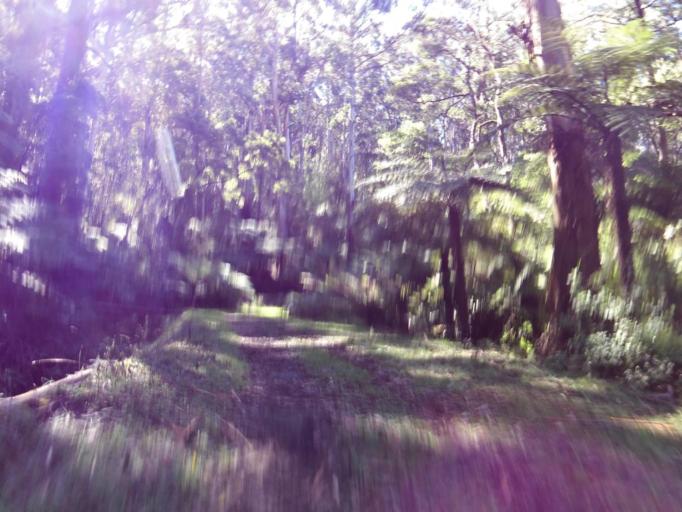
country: AU
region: Victoria
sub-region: Yarra Ranges
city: Millgrove
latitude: -37.7419
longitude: 145.6271
